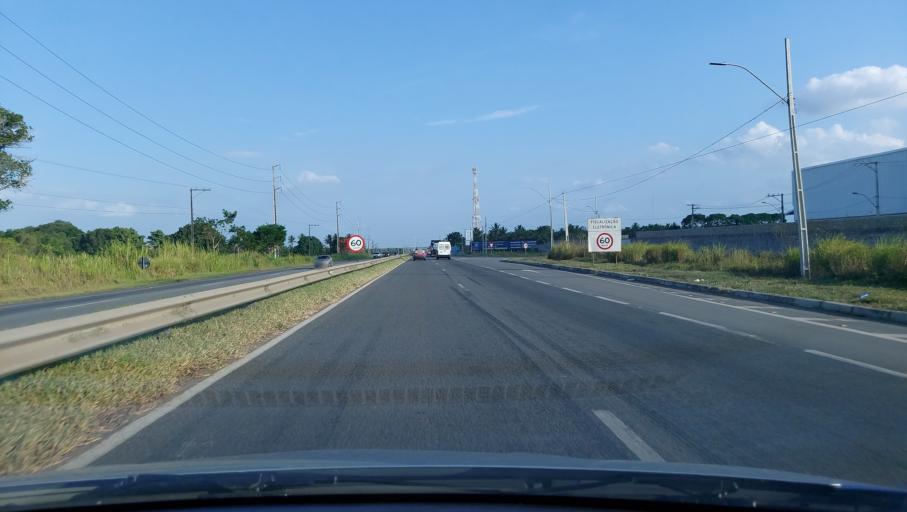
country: BR
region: Bahia
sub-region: Conceicao Do Jacuipe
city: Conceicao do Jacuipe
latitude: -12.3737
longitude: -38.8076
